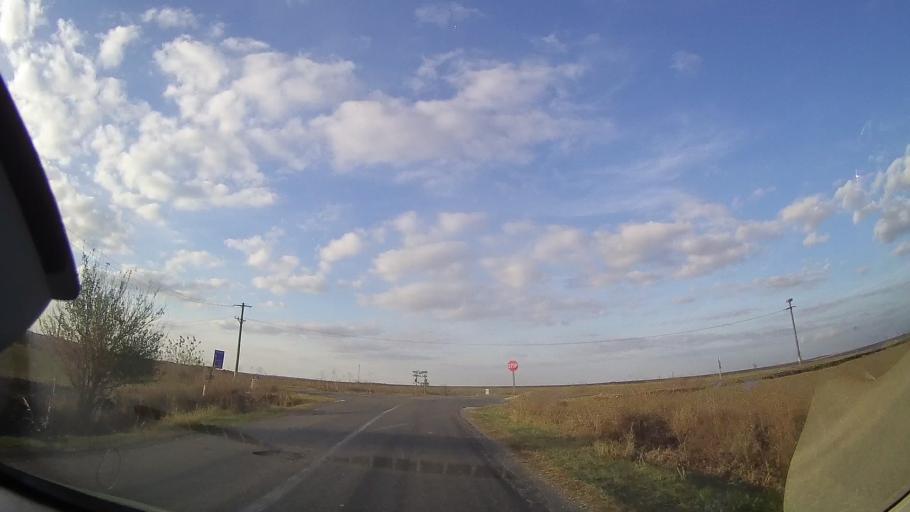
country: RO
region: Constanta
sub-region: Comuna Dumbraveni
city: Dumbraveni
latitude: 43.9335
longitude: 28.0250
